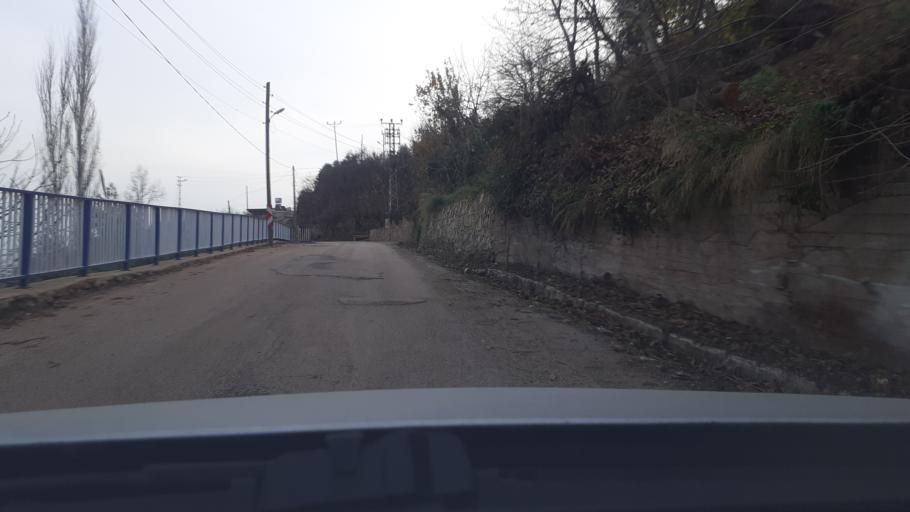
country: TR
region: Hatay
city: Kirikhan
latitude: 36.5353
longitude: 36.3143
